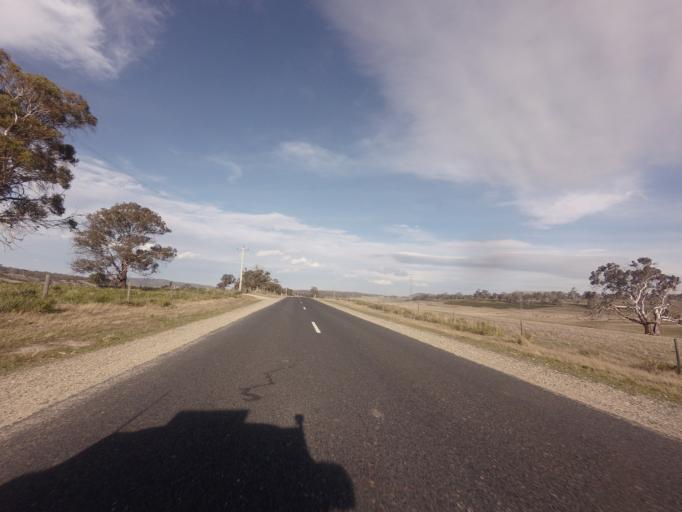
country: AU
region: Tasmania
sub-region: Derwent Valley
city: New Norfolk
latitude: -42.2515
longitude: 146.9297
